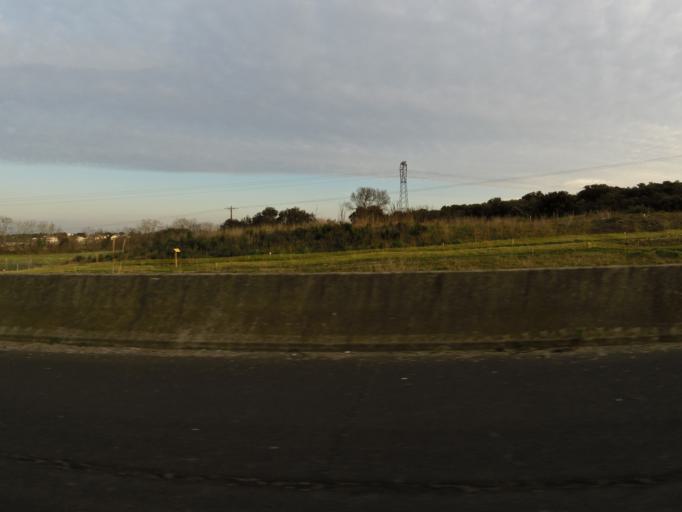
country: FR
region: Languedoc-Roussillon
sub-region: Departement de l'Herault
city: Baillargues
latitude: 43.6736
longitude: 4.0194
